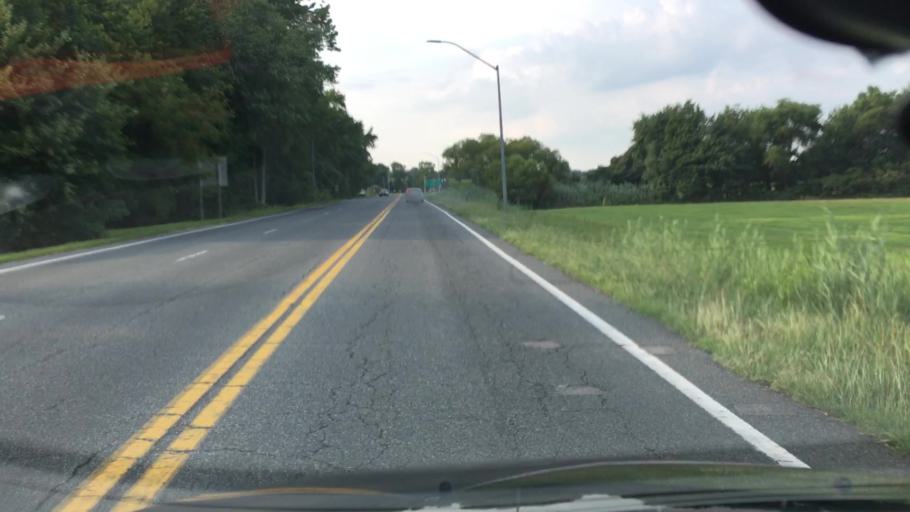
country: US
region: Maryland
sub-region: Worcester County
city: Ocean Pines
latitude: 38.3481
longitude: -75.1679
